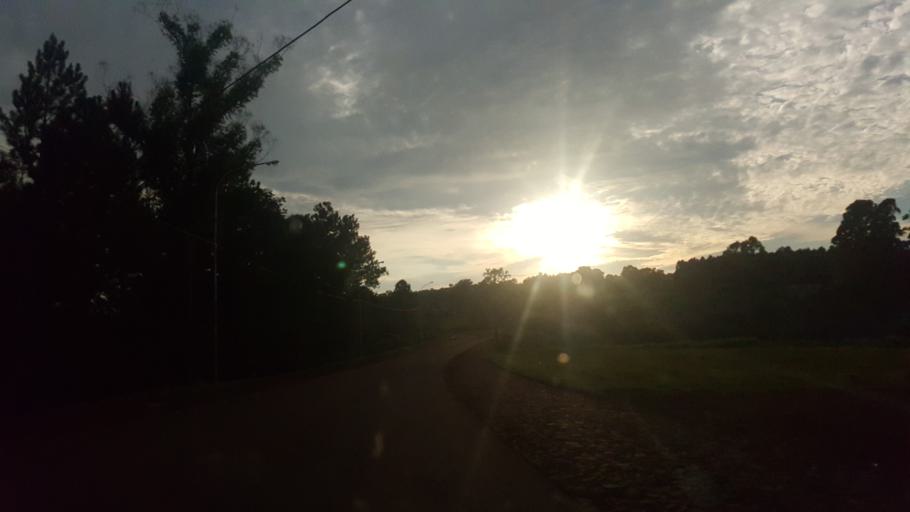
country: AR
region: Misiones
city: Dos de Mayo
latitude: -27.0358
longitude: -54.6785
